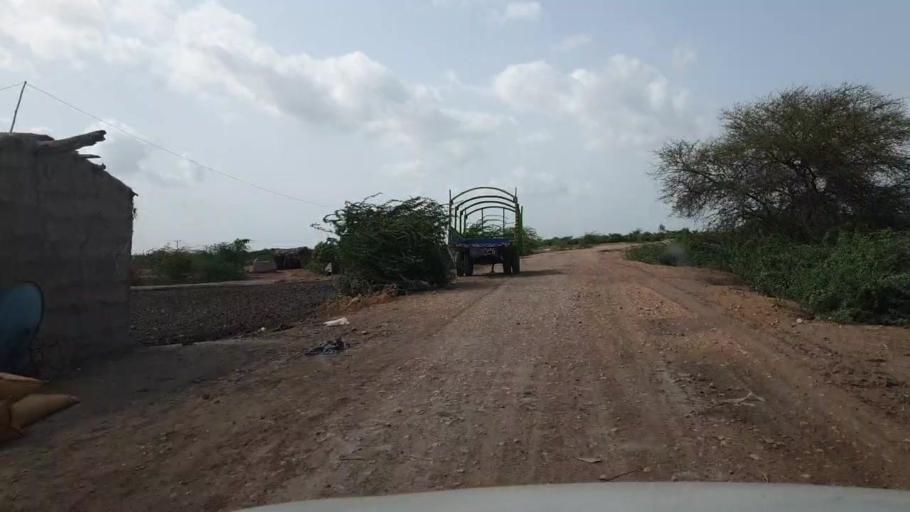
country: PK
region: Sindh
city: Kario
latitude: 24.7092
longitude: 68.6432
